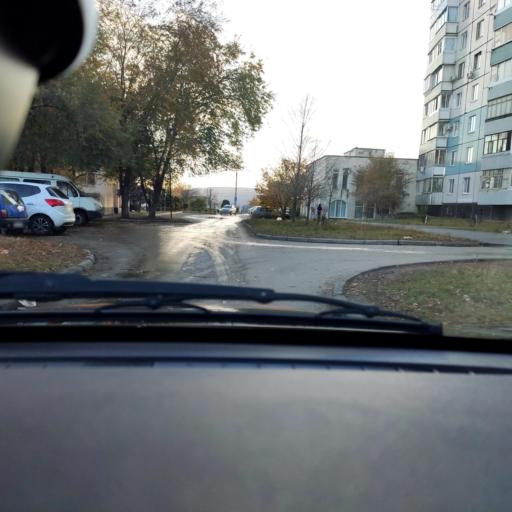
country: RU
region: Samara
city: Zhigulevsk
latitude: 53.4767
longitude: 49.4640
